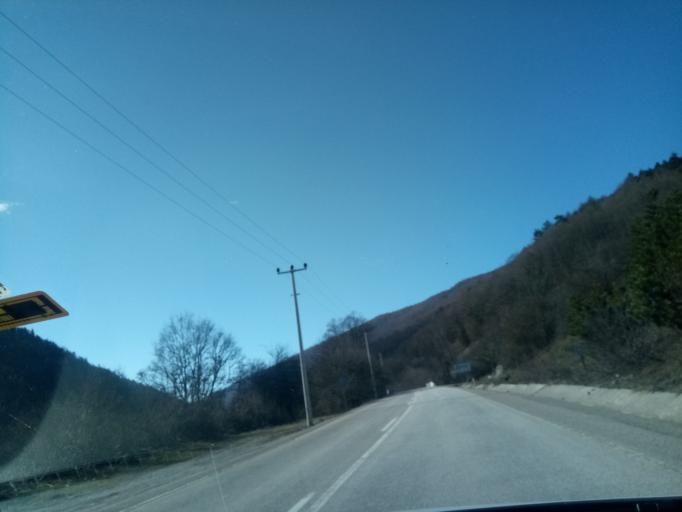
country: TR
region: Duzce
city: Kaynasli
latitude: 40.6604
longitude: 31.4040
